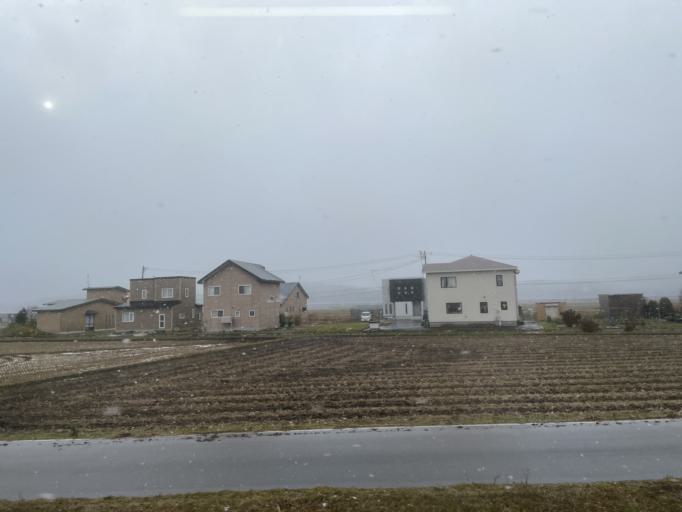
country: JP
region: Aomori
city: Aomori Shi
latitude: 40.9129
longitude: 140.6687
